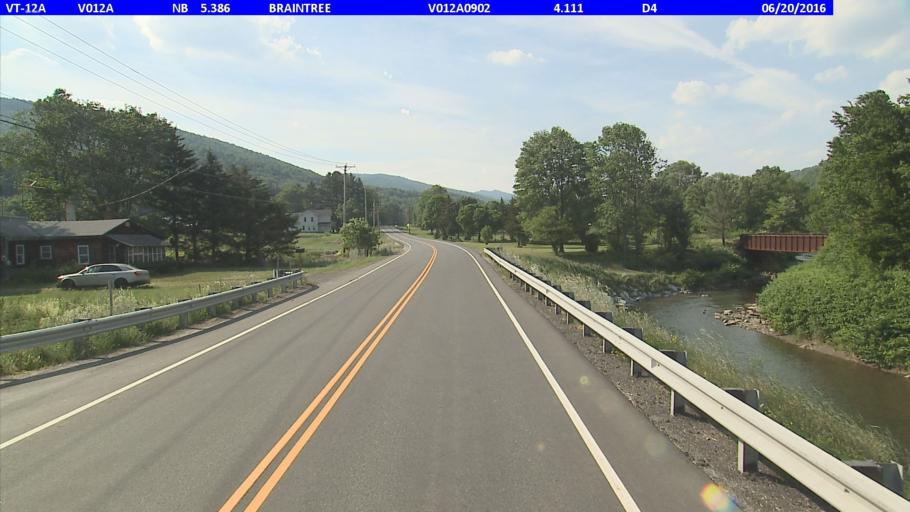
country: US
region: Vermont
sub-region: Orange County
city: Randolph
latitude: 43.9677
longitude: -72.7445
